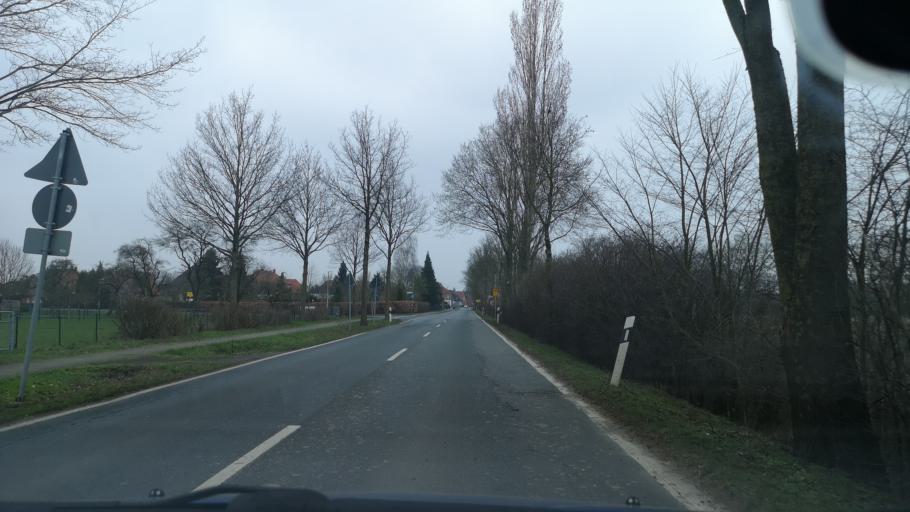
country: DE
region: Lower Saxony
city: Schwarmstedt
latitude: 52.5946
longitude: 9.5703
